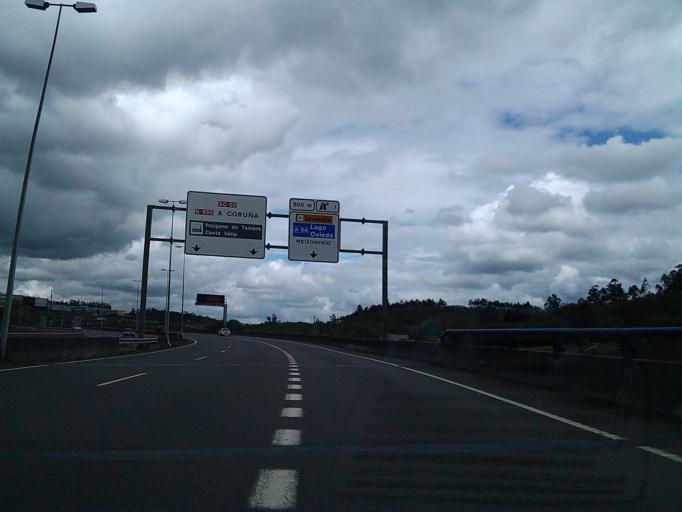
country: ES
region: Galicia
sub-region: Provincia da Coruna
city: Santiago de Compostela
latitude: 42.8925
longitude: -8.5070
